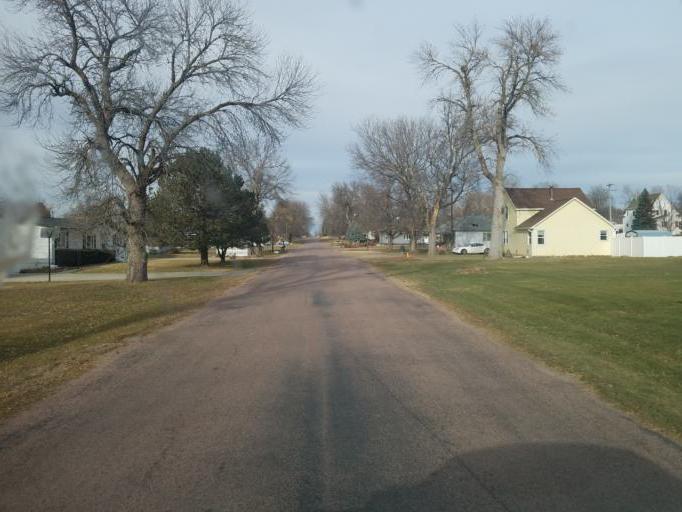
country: US
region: Nebraska
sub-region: Knox County
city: Creighton
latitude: 42.4611
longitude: -97.9091
